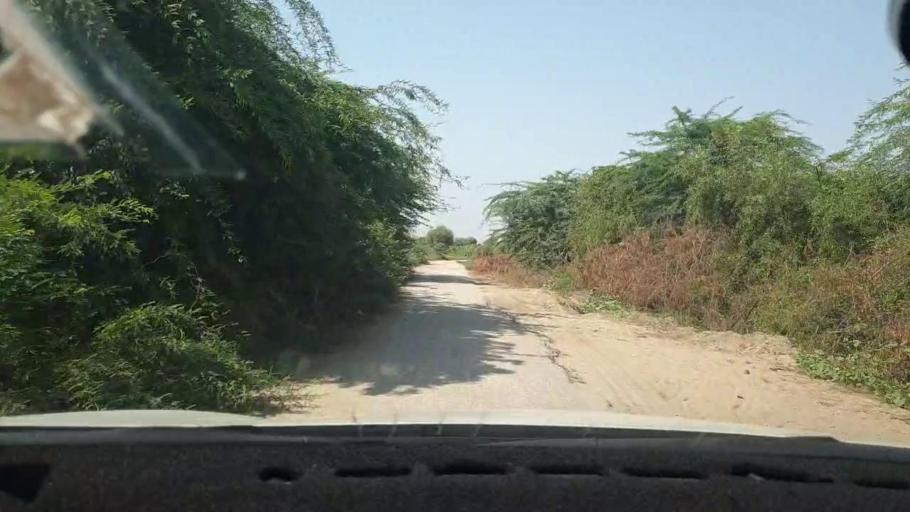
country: PK
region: Sindh
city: Tando Mittha Khan
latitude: 25.8630
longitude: 69.3851
